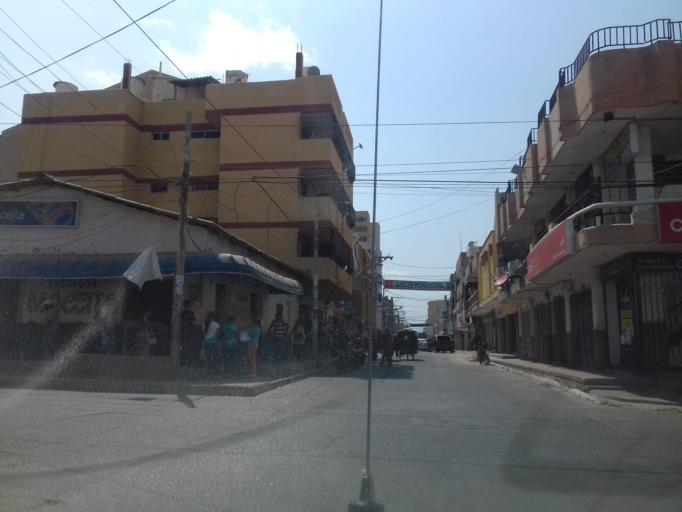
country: CO
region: La Guajira
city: Maicao
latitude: 11.3788
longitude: -72.2364
